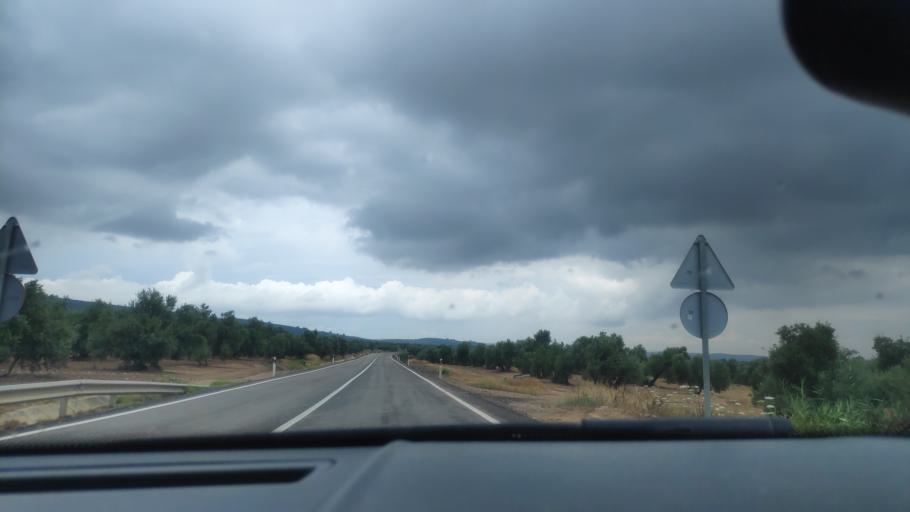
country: ES
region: Andalusia
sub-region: Provincia de Jaen
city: Jabalquinto
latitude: 38.0362
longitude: -3.7560
